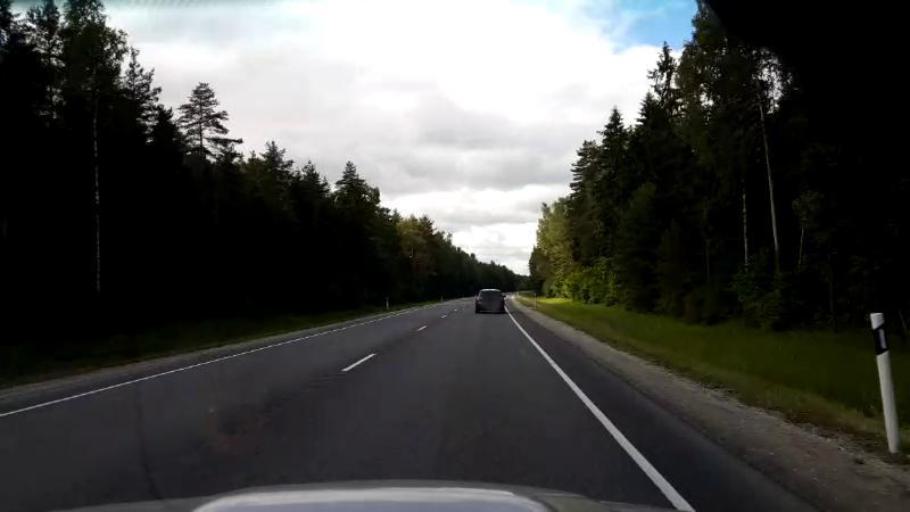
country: EE
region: Raplamaa
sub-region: Maerjamaa vald
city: Marjamaa
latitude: 58.8897
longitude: 24.4537
